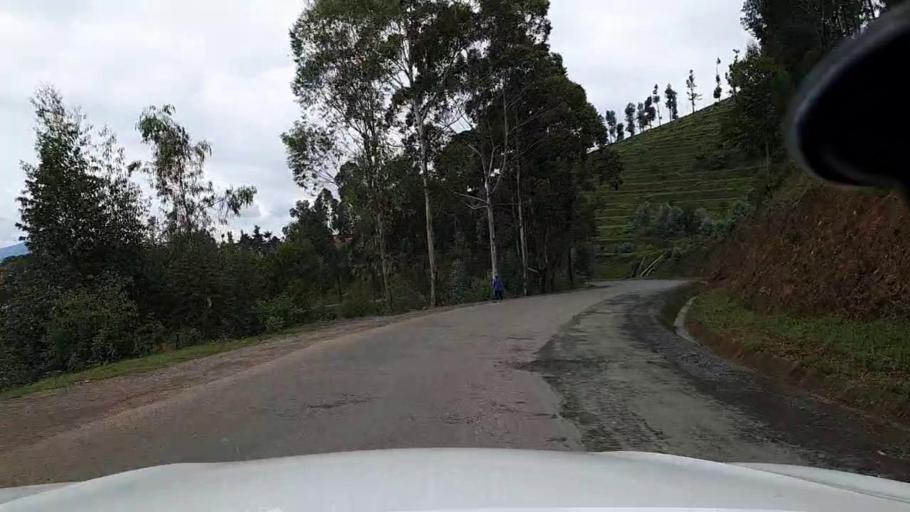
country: RW
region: Western Province
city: Kibuye
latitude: -2.0671
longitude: 29.5392
